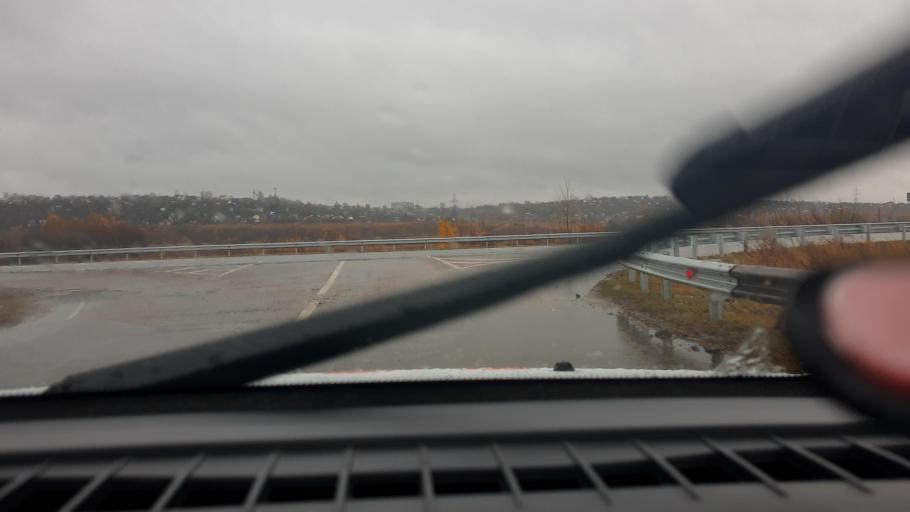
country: RU
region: Nizjnij Novgorod
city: Kstovo
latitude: 56.1447
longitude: 44.1572
